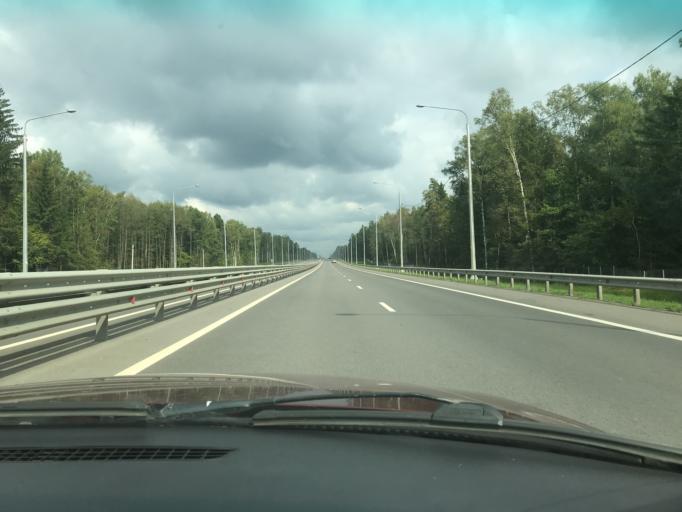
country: RU
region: Kaluga
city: Pyatovskiy
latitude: 54.6513
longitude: 36.1377
